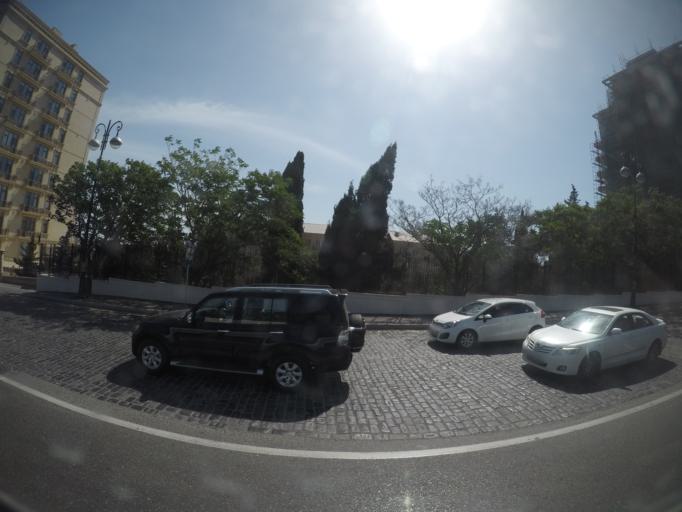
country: AZ
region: Baki
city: Badamdar
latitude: 40.3623
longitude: 49.8266
